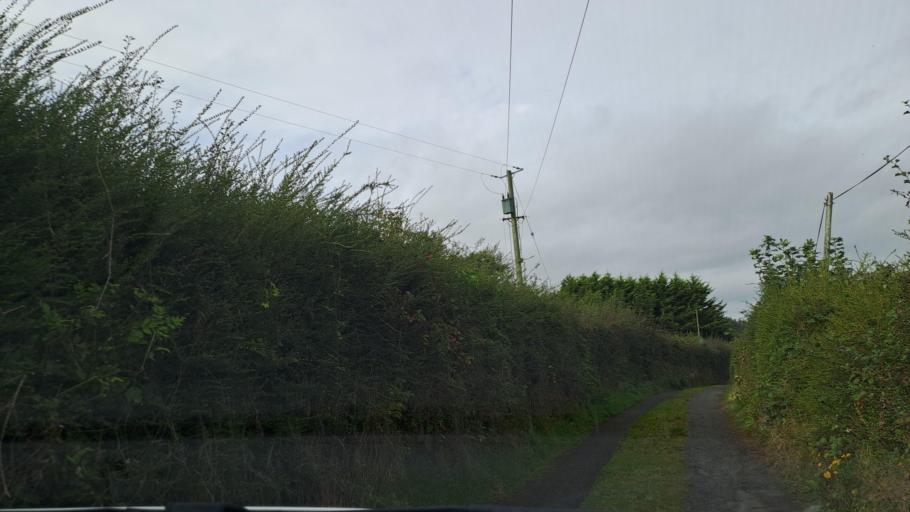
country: IE
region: Ulster
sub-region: An Cabhan
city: Bailieborough
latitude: 54.0039
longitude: -6.9467
